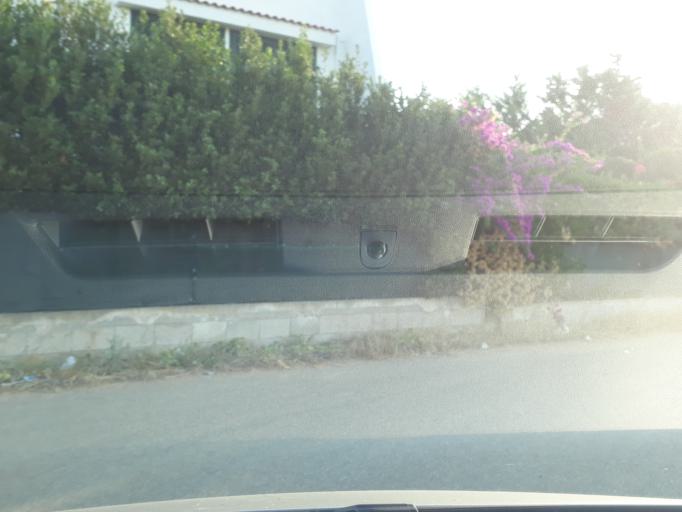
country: IT
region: Apulia
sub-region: Provincia di Brindisi
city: Carovigno
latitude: 40.7519
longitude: 17.7087
